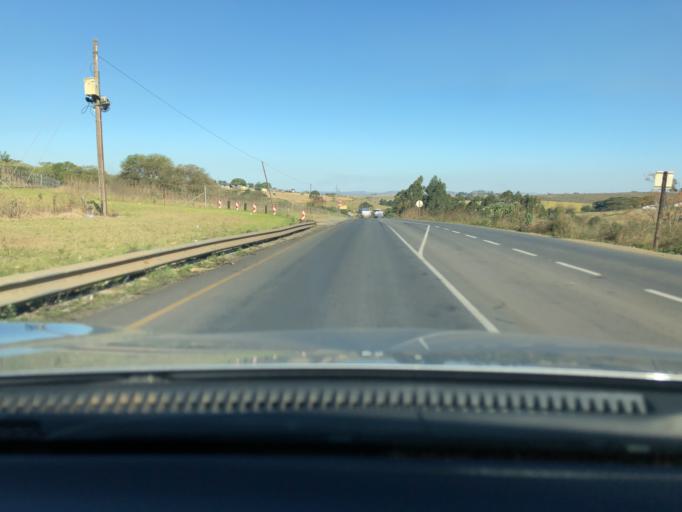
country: ZA
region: KwaZulu-Natal
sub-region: uMgungundlovu District Municipality
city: Camperdown
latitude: -29.7342
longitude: 30.5076
